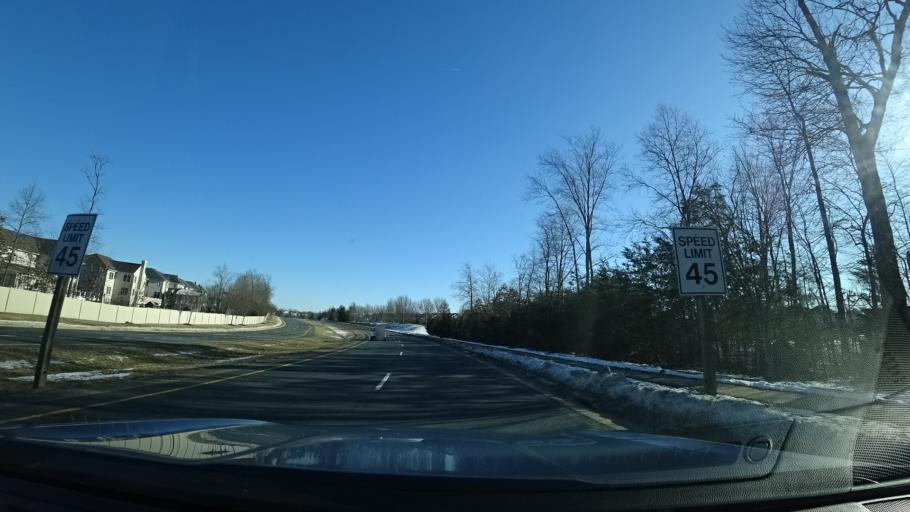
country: US
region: Virginia
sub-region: Loudoun County
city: Belmont
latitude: 39.0550
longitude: -77.5002
